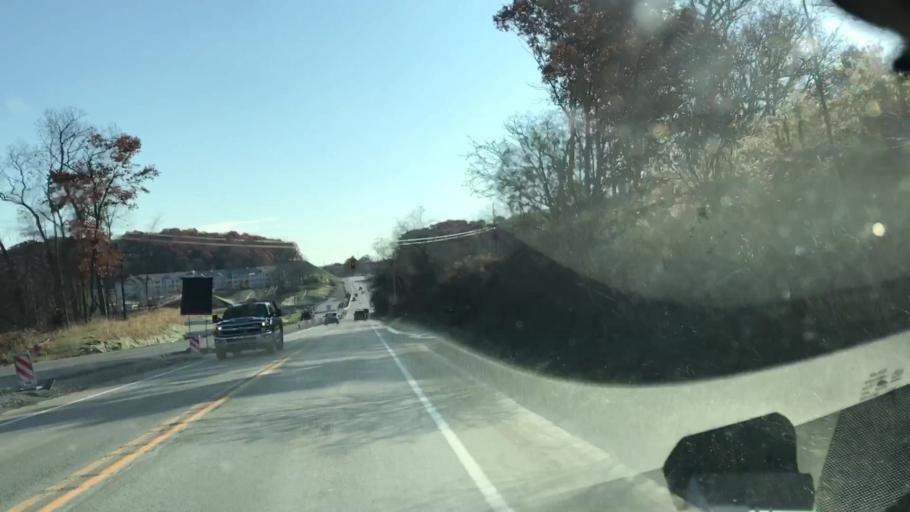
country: US
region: Pennsylvania
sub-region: Butler County
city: Mars
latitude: 40.6927
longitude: -80.0226
